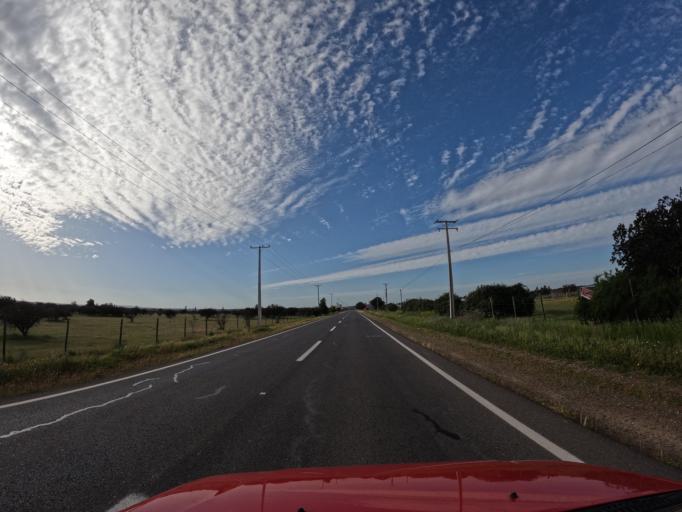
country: CL
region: Valparaiso
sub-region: San Antonio Province
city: San Antonio
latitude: -34.1593
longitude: -71.7321
